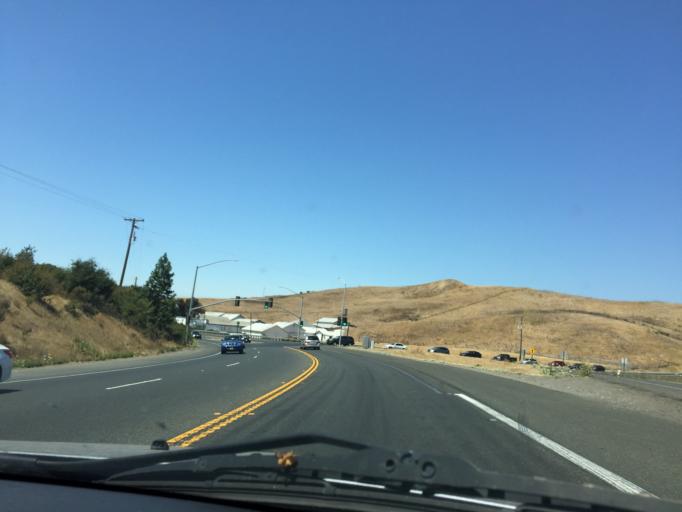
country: US
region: California
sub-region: Sonoma County
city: Sonoma
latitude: 38.2534
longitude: -122.3922
